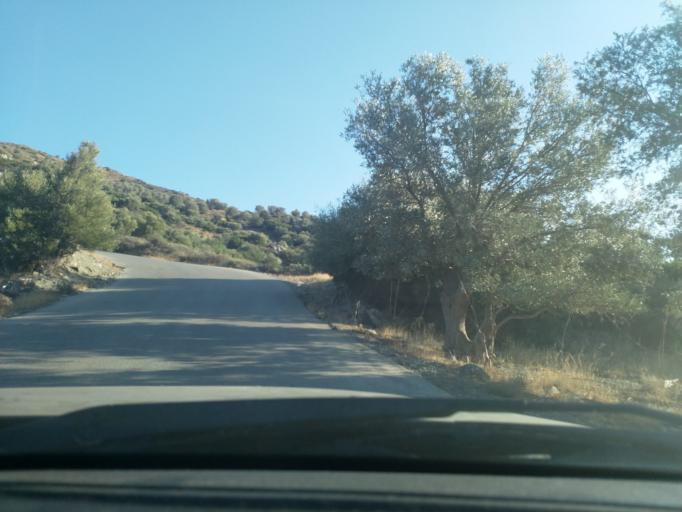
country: GR
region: Crete
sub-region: Nomos Rethymnis
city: Agia Galini
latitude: 35.1144
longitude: 24.5660
